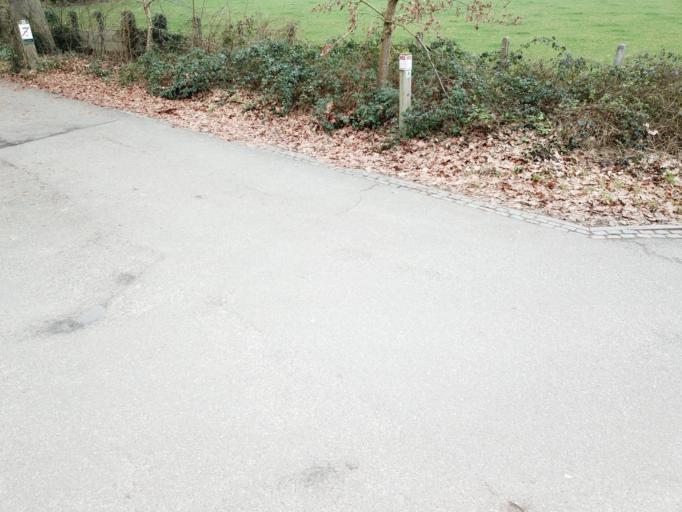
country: BE
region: Flanders
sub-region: Provincie Vlaams-Brabant
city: Leuven
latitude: 50.8482
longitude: 4.7027
